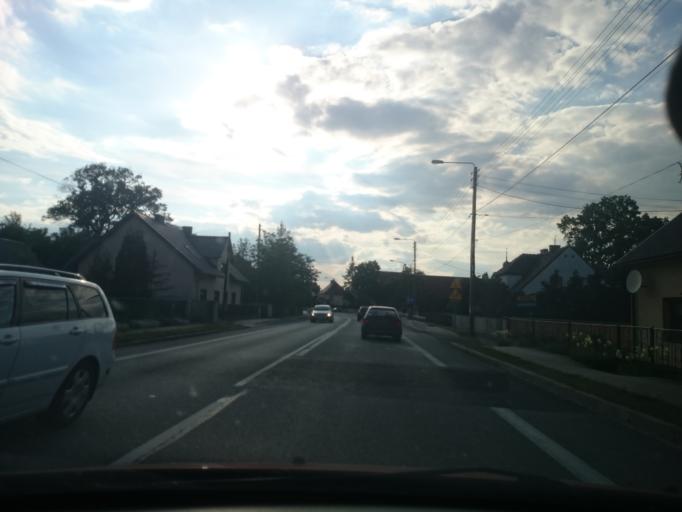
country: PL
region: Opole Voivodeship
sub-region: Powiat opolski
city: Naklo
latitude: 50.5791
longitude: 18.1217
